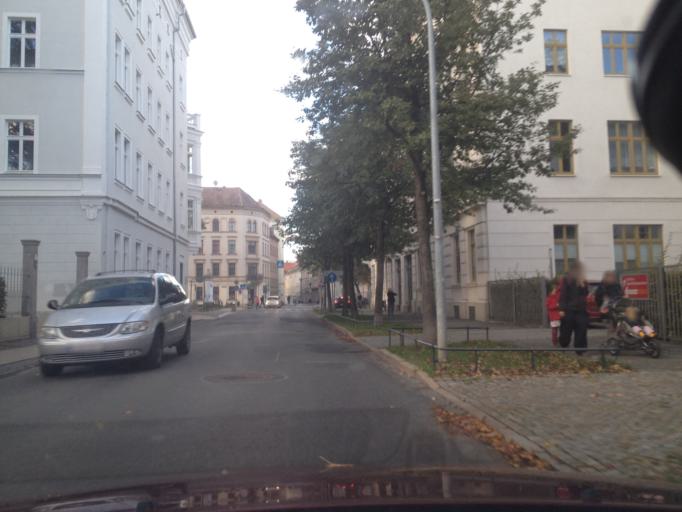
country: DE
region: Saxony
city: Goerlitz
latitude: 51.1539
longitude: 14.9925
